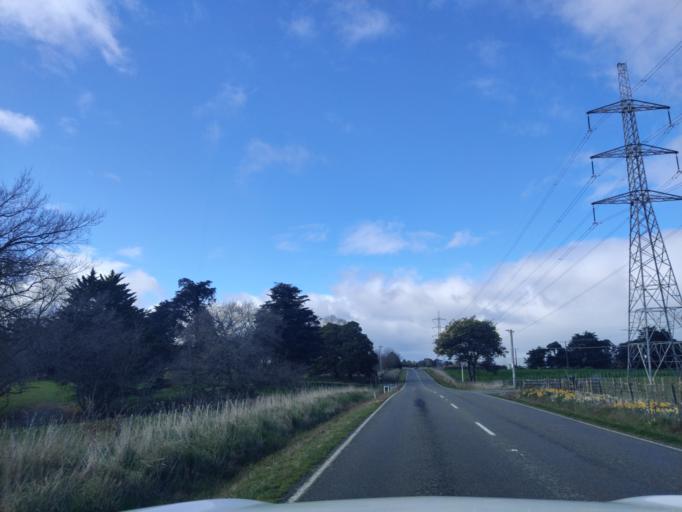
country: NZ
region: Manawatu-Wanganui
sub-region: Palmerston North City
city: Palmerston North
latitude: -40.2852
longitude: 175.6621
